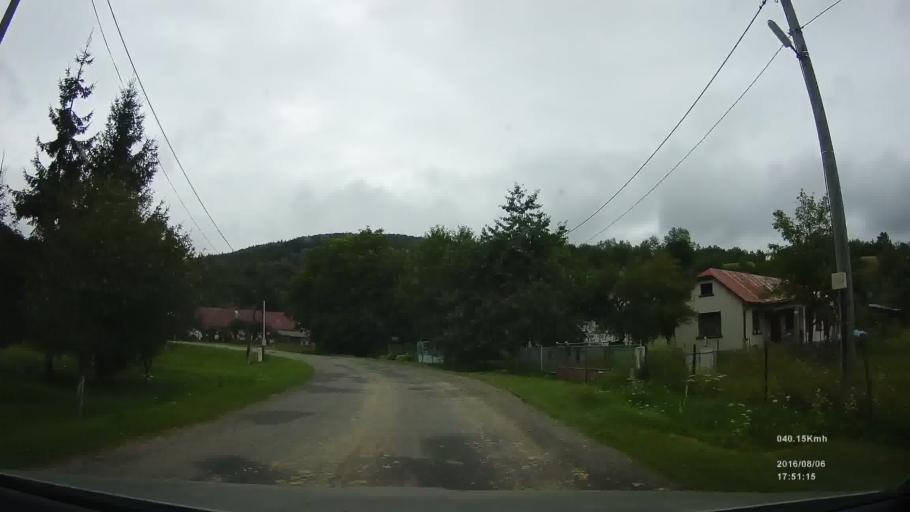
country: SK
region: Presovsky
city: Svidnik
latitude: 49.3993
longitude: 21.5706
